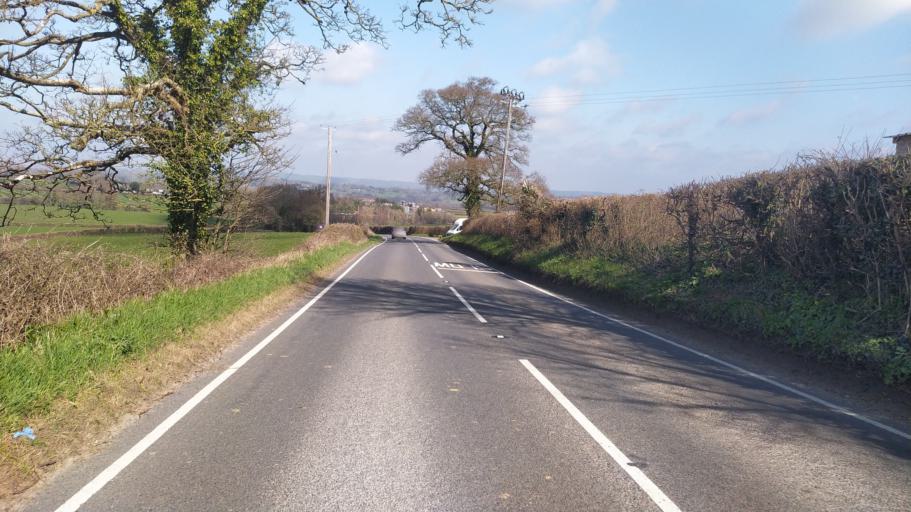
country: GB
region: England
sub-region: Somerset
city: Crewkerne
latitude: 50.8552
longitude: -2.7733
